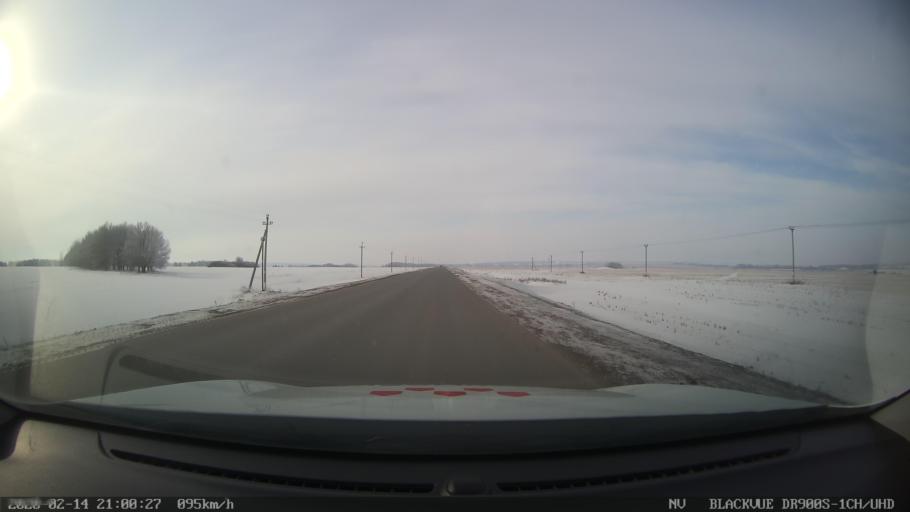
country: RU
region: Tatarstan
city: Kuybyshevskiy Zaton
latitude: 55.1711
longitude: 49.2197
